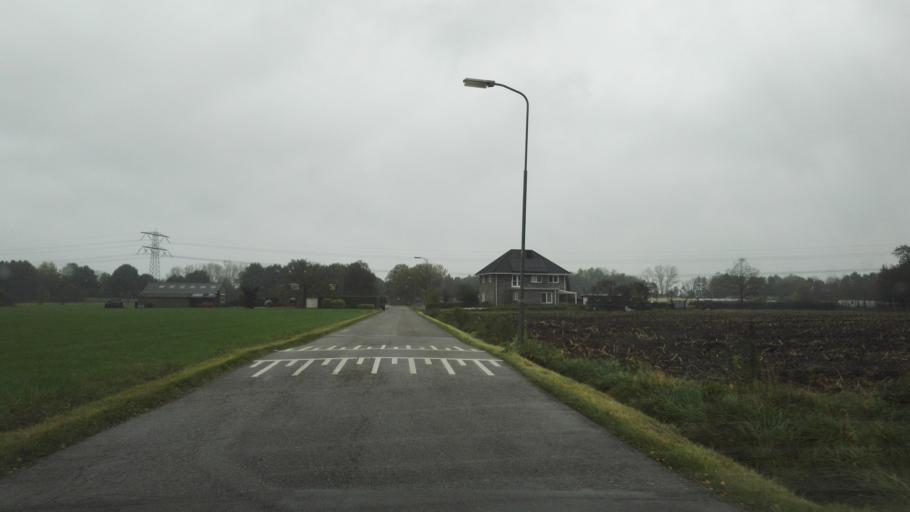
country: NL
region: Gelderland
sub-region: Gemeente Apeldoorn
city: Apeldoorn
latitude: 52.2308
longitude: 6.0095
